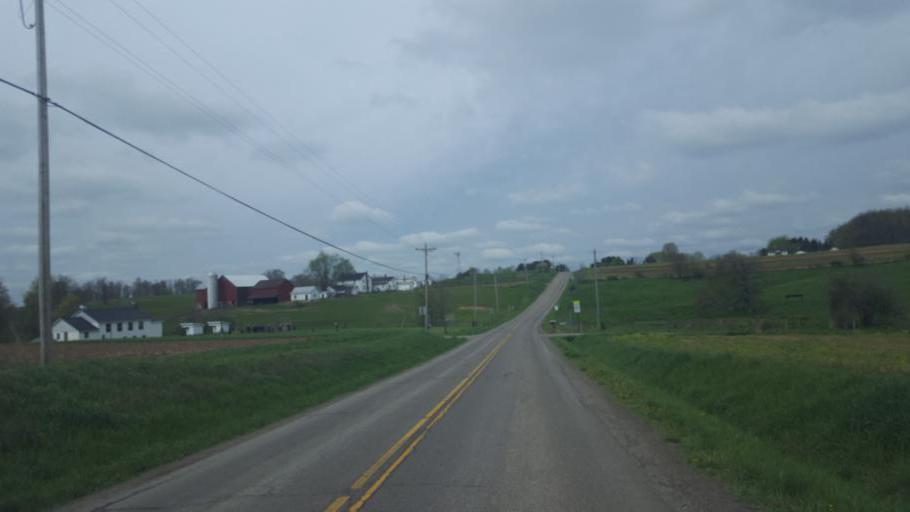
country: US
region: Ohio
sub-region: Wayne County
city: Apple Creek
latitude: 40.6954
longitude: -81.8074
